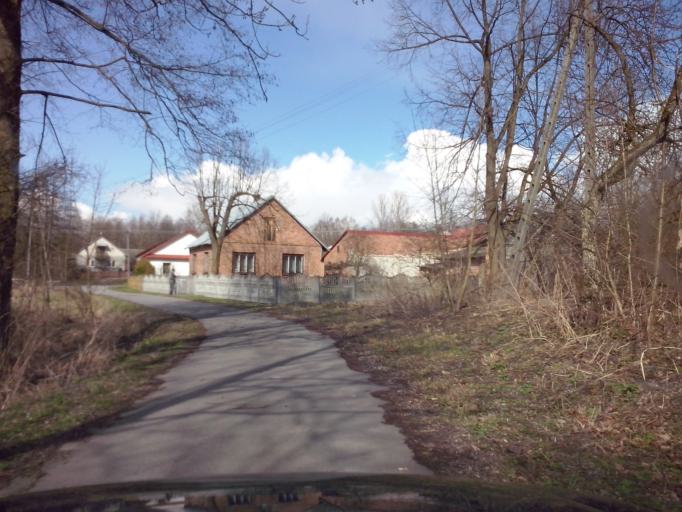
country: PL
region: Subcarpathian Voivodeship
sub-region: Powiat nizanski
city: Bieliny
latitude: 50.4406
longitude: 22.3046
